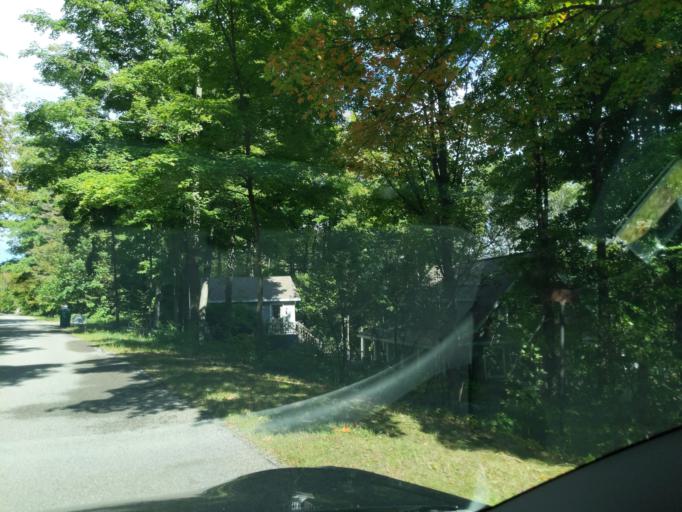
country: US
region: Michigan
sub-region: Antrim County
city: Bellaire
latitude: 44.9722
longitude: -85.3235
